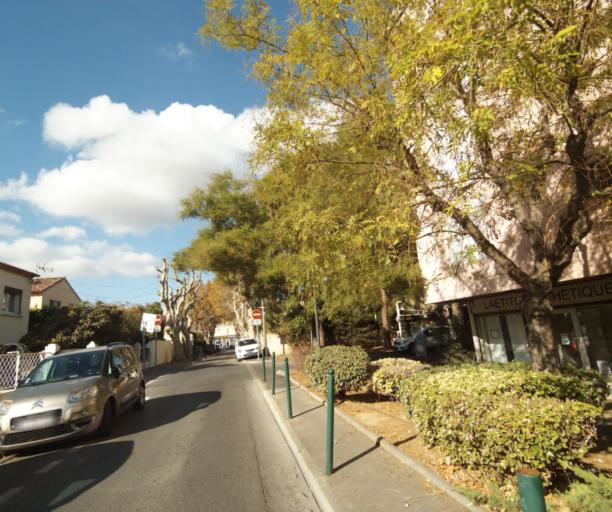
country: FR
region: Provence-Alpes-Cote d'Azur
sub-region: Departement des Bouches-du-Rhone
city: Plan-de-Cuques
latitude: 43.3458
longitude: 5.4636
